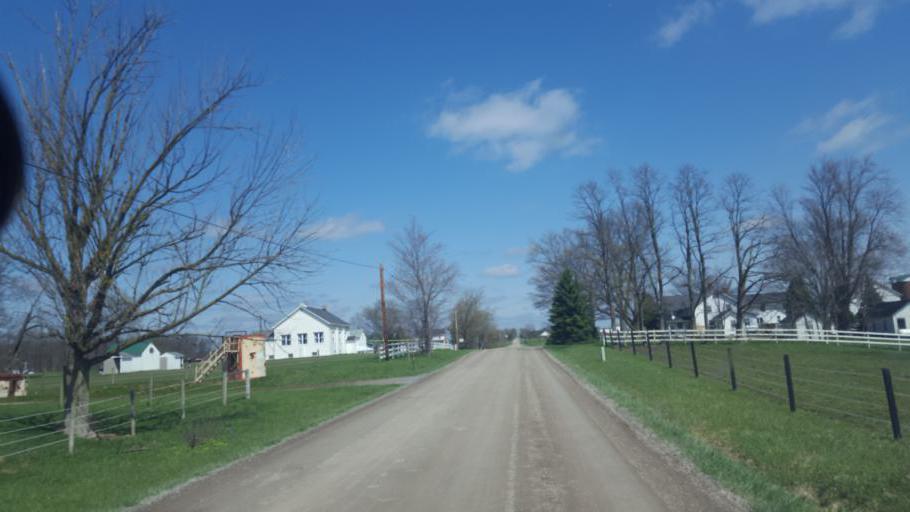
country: US
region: Ohio
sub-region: Geauga County
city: Middlefield
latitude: 41.4027
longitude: -81.0802
